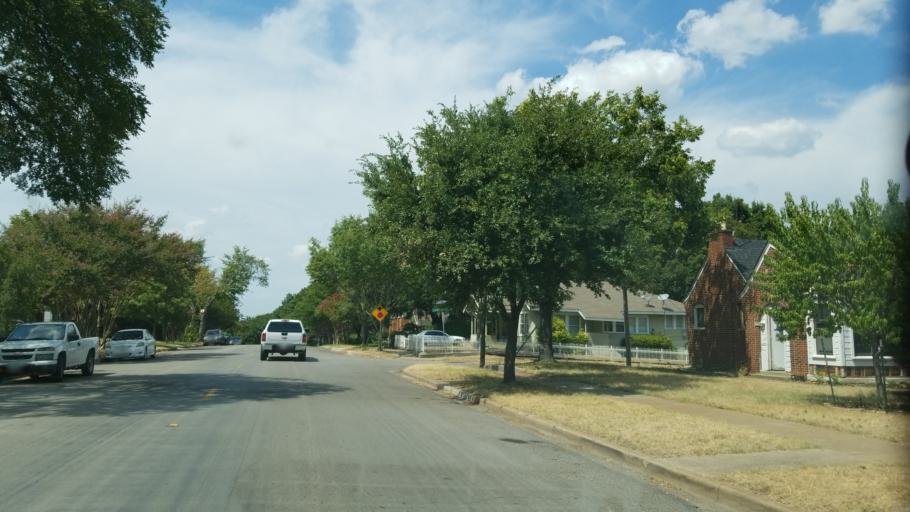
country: US
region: Texas
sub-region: Dallas County
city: Cockrell Hill
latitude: 32.7540
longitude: -96.8453
